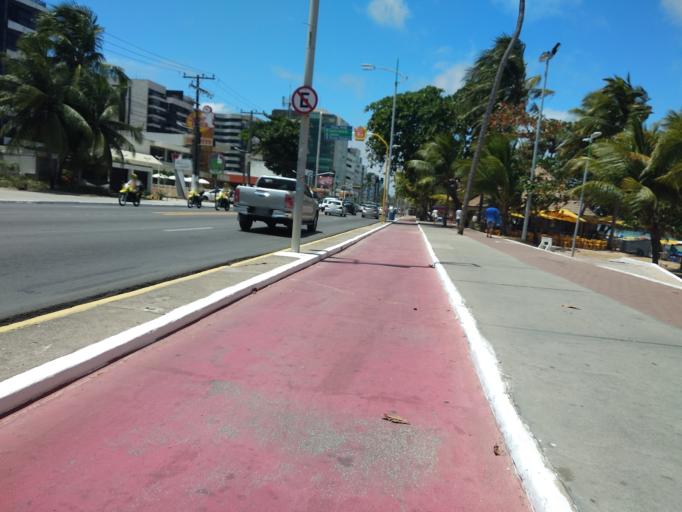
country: BR
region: Alagoas
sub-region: Maceio
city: Maceio
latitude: -9.6576
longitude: -35.6984
